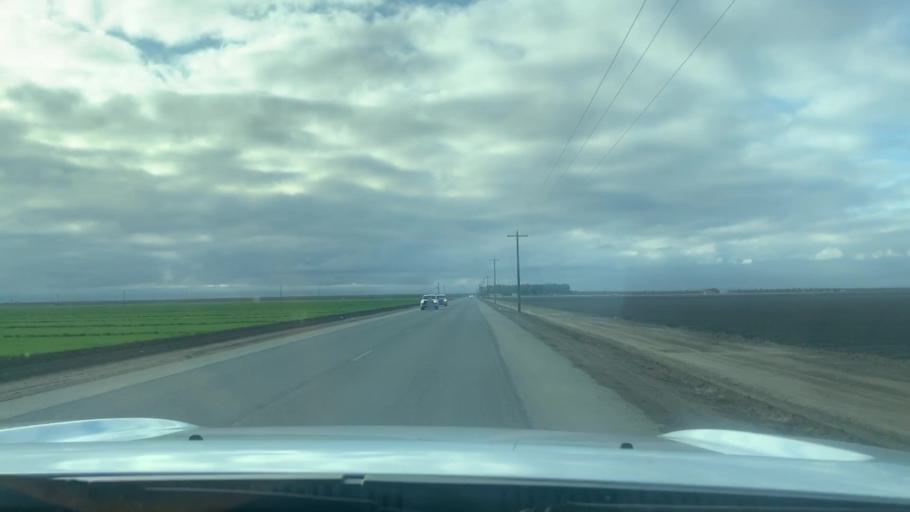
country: US
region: California
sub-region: Kern County
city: Buttonwillow
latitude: 35.5006
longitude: -119.4587
